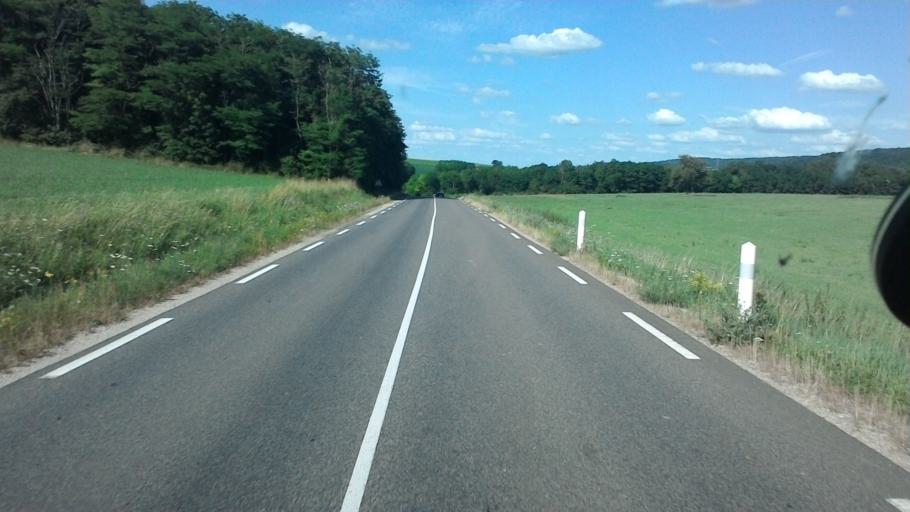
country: FR
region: Franche-Comte
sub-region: Departement de la Haute-Saone
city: Gy
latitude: 47.3753
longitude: 5.7669
